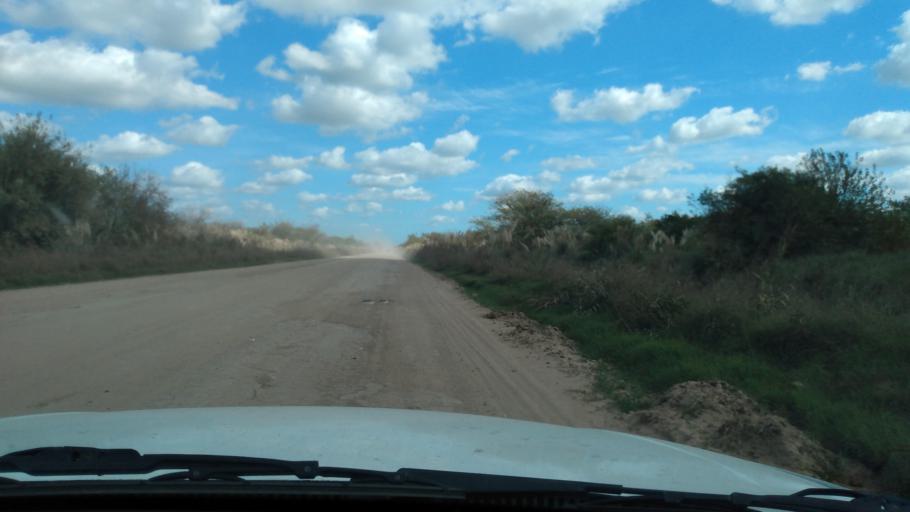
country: AR
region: Buenos Aires
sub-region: Partido de Navarro
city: Navarro
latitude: -34.9981
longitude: -59.3215
